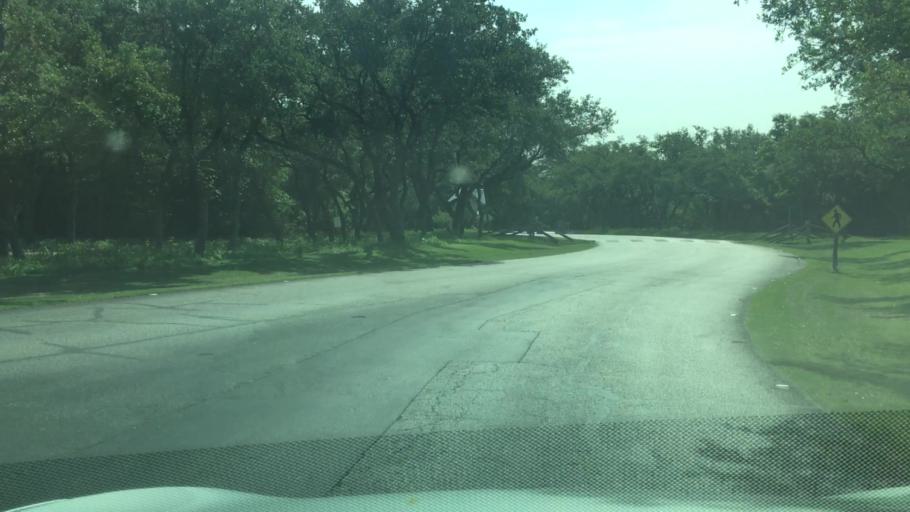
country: US
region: Texas
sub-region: Bexar County
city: Leon Valley
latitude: 29.4604
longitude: -98.6848
